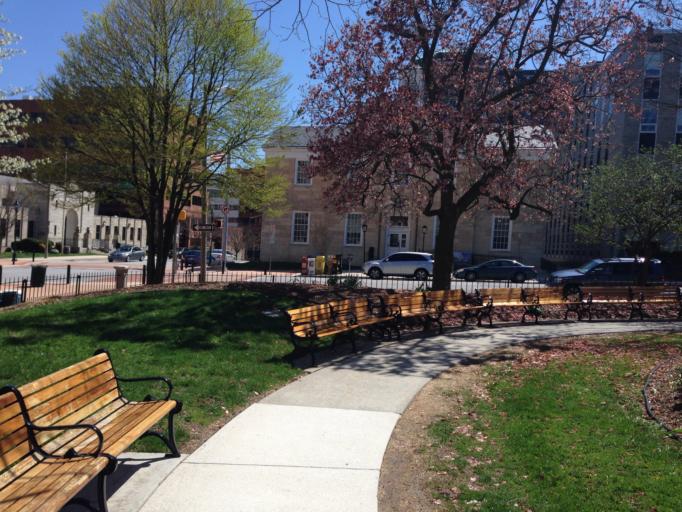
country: US
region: Maryland
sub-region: Baltimore County
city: Towson
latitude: 39.4000
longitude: -76.6057
